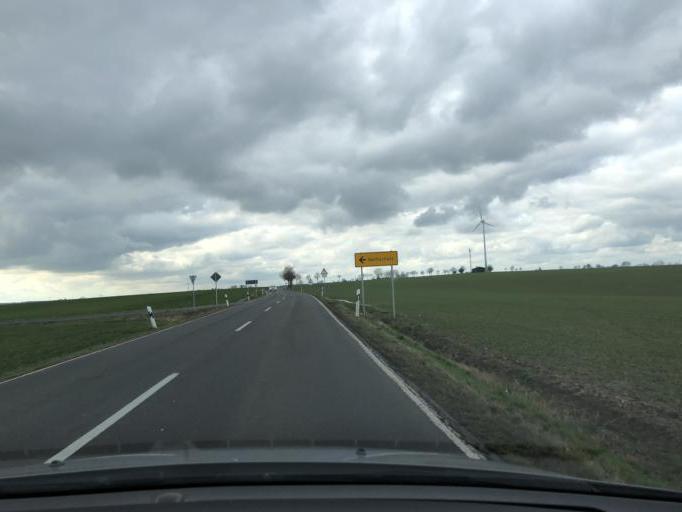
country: DE
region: Saxony
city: Grossweitzschen
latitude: 51.1518
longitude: 13.0823
